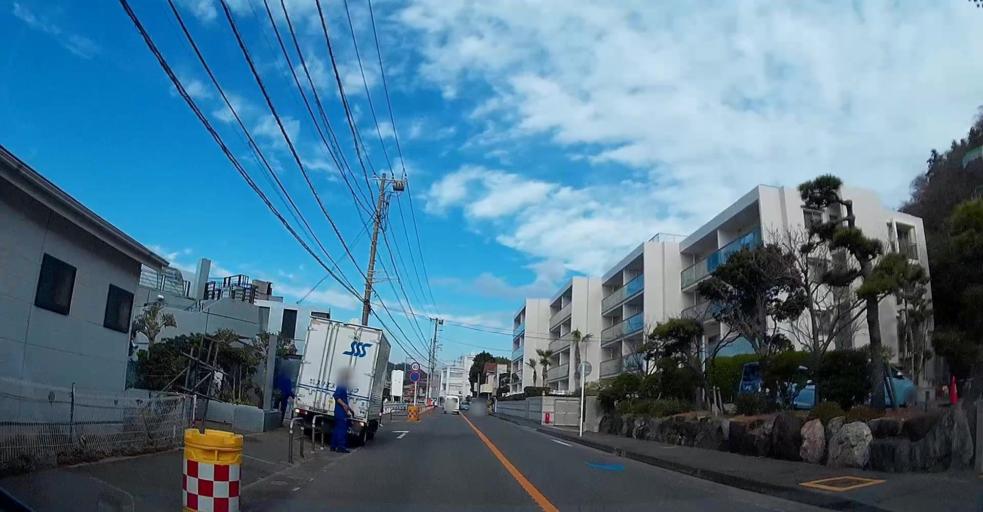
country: JP
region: Kanagawa
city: Hayama
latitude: 35.2686
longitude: 139.5705
